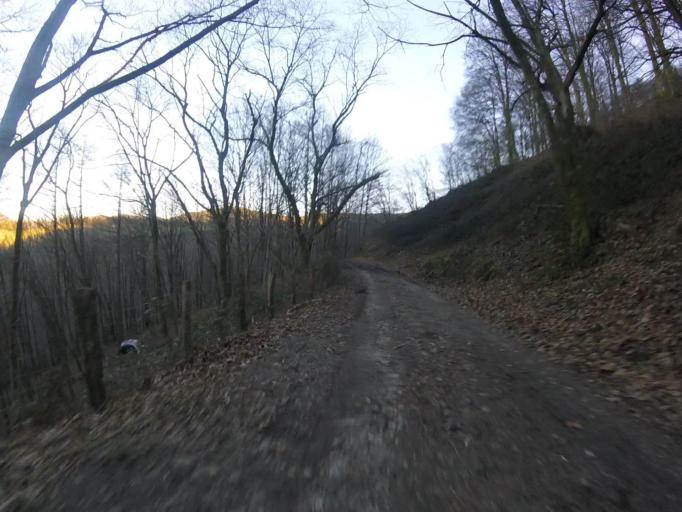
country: ES
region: Basque Country
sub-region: Provincia de Guipuzcoa
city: Irun
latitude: 43.2611
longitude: -1.8266
